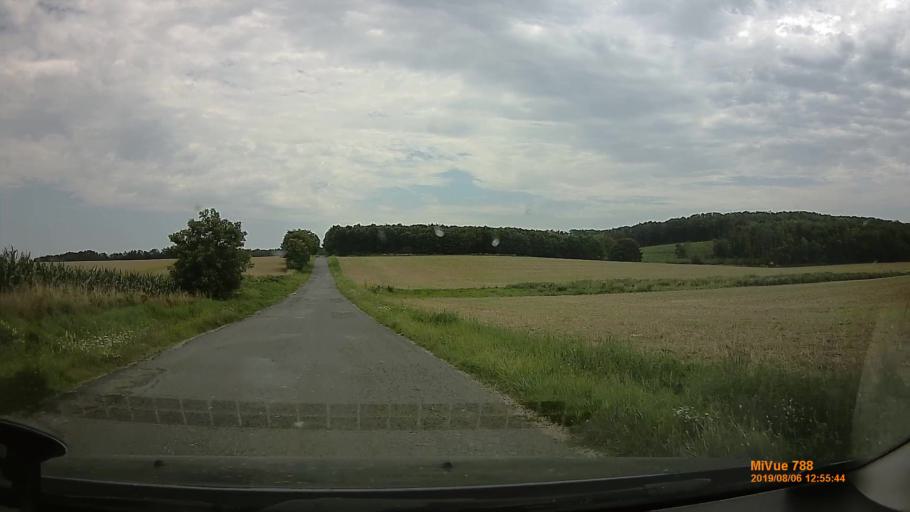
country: HU
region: Zala
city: Pacsa
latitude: 46.6359
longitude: 17.0204
